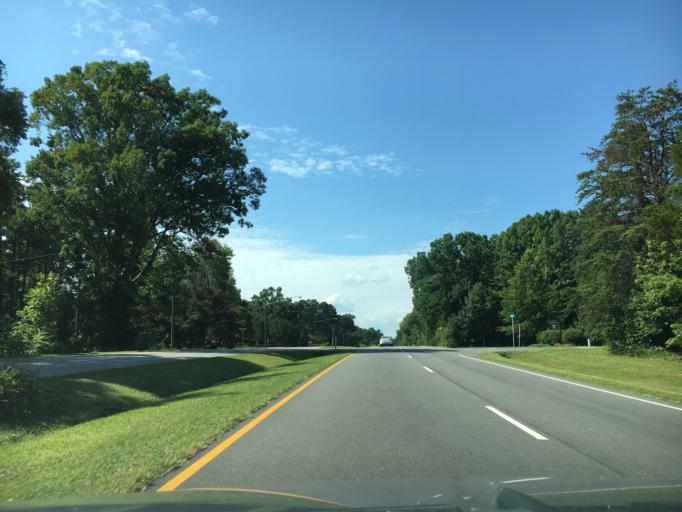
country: US
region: Virginia
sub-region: Halifax County
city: South Boston
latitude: 36.7201
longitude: -78.9177
